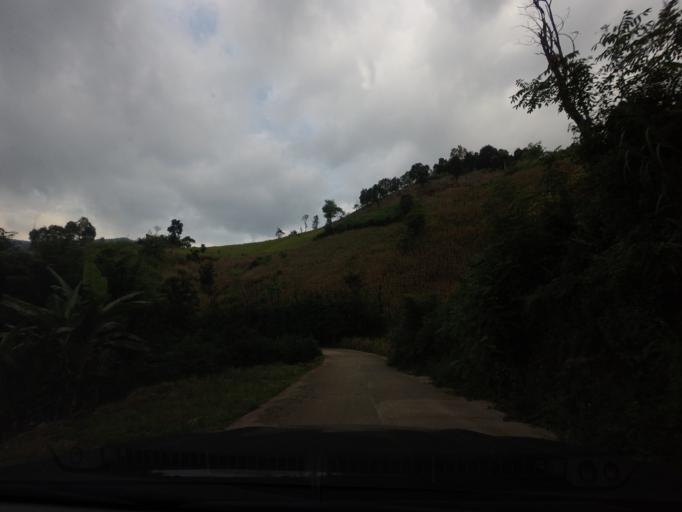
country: TH
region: Nan
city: Bo Kluea
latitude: 19.3512
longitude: 101.1691
